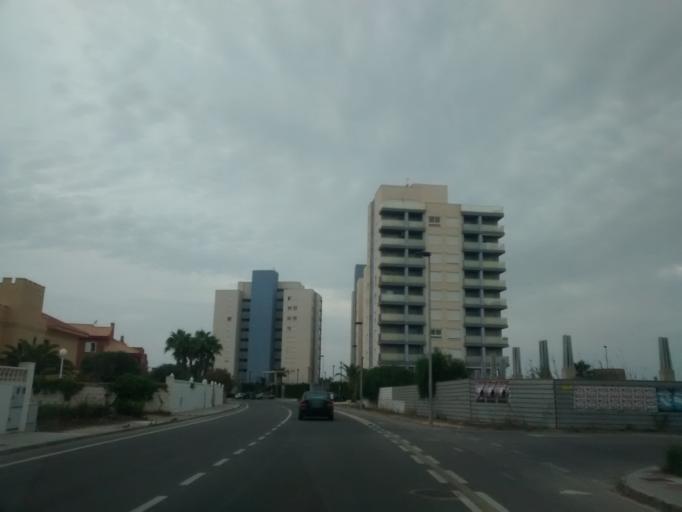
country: ES
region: Murcia
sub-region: Murcia
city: San Pedro del Pinatar
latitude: 37.7759
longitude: -0.7445
